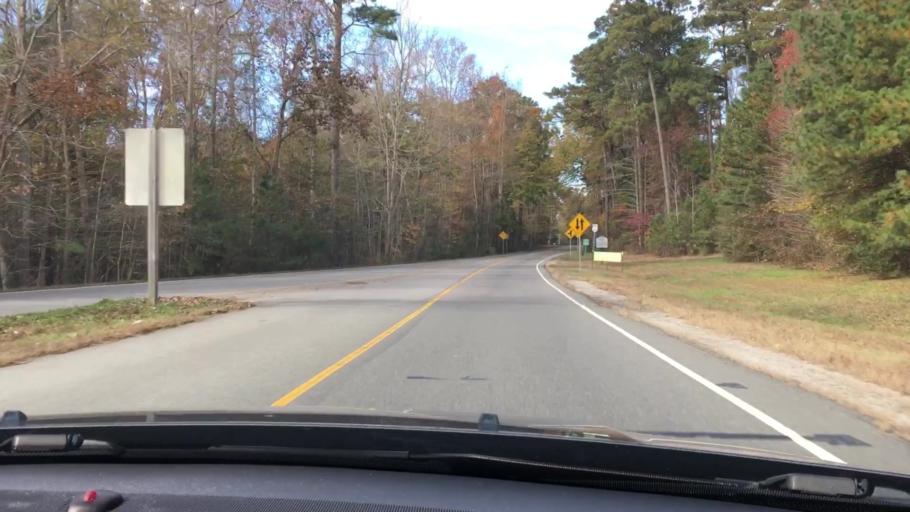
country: US
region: Virginia
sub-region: King William County
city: West Point
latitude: 37.4299
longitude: -76.8306
